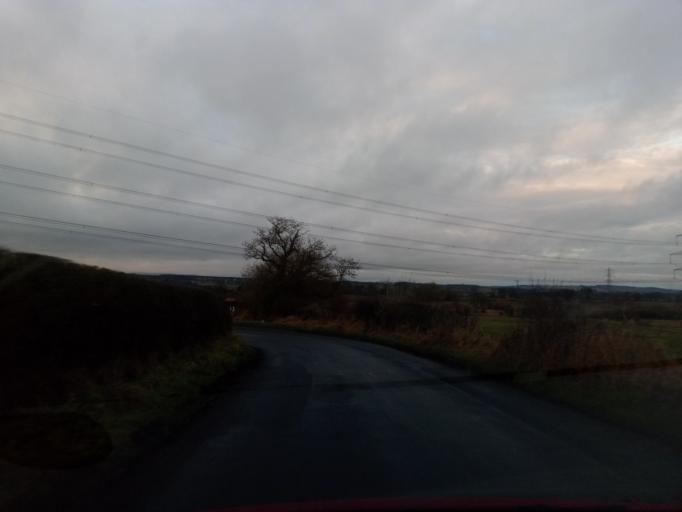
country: GB
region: England
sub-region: Northumberland
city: Meldon
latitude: 55.1434
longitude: -1.8047
